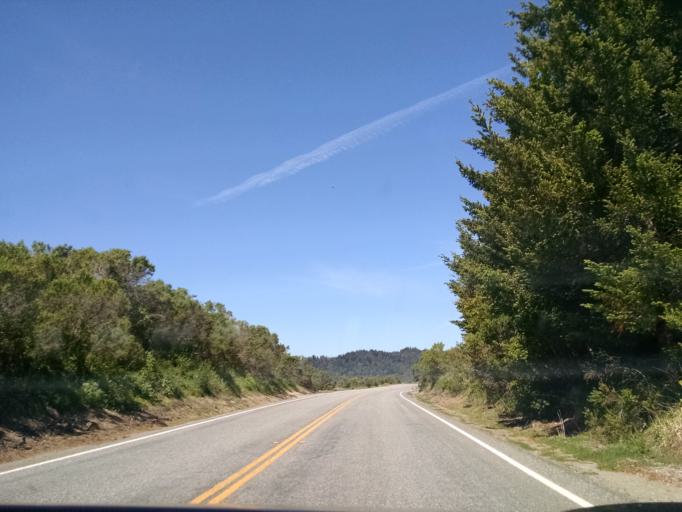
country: US
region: California
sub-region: San Mateo County
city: Portola Valley
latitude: 37.3570
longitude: -122.2454
